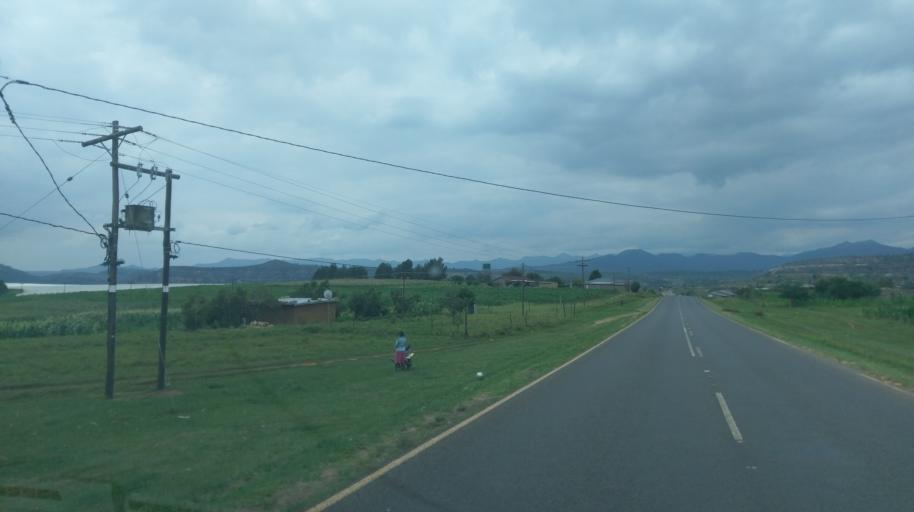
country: LS
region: Leribe
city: Leribe
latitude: -28.9358
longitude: 28.1551
